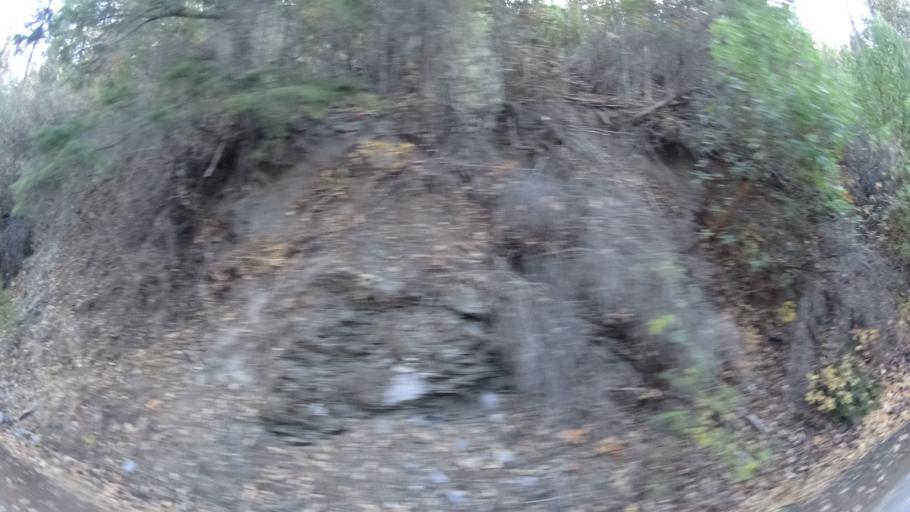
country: US
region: California
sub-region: Siskiyou County
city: Yreka
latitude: 41.8408
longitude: -122.9157
